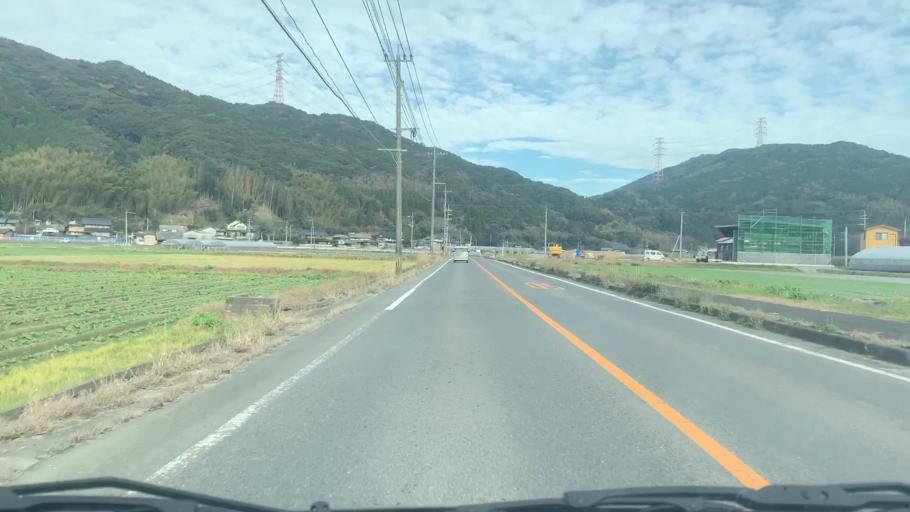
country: JP
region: Saga Prefecture
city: Karatsu
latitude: 33.3781
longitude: 129.9994
